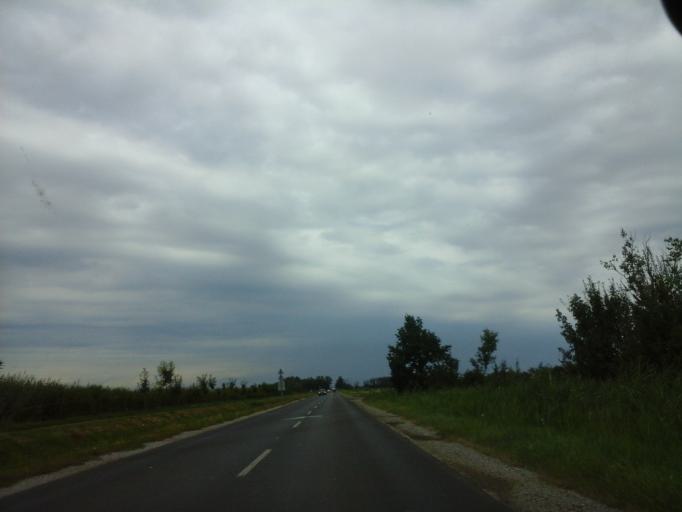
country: HU
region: Hajdu-Bihar
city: Balmazujvaros
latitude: 47.5843
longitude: 21.3471
